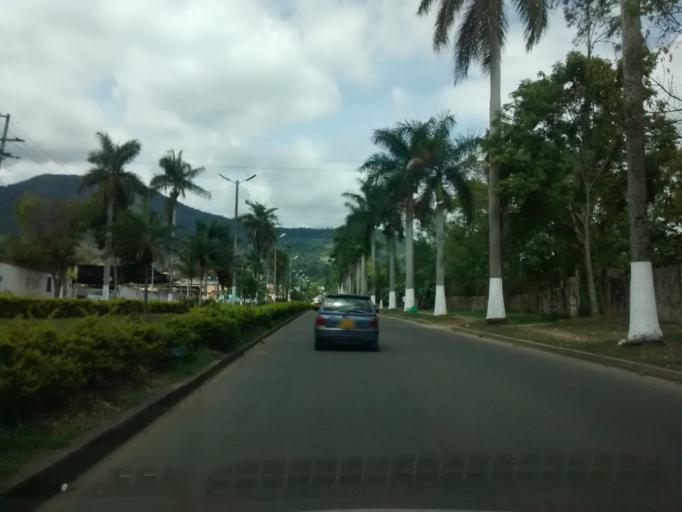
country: CO
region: Cundinamarca
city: Fusagasuga
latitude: 4.3430
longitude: -74.3713
